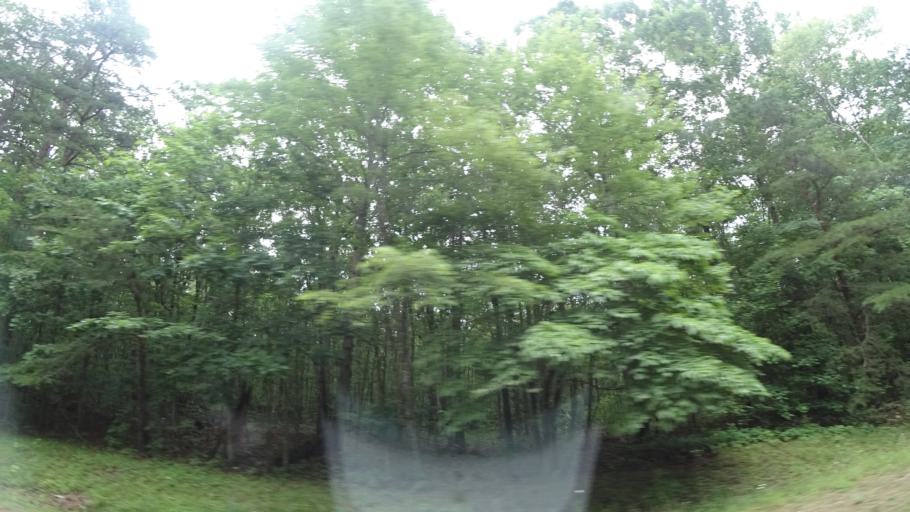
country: US
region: Virginia
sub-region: Louisa County
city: Louisa
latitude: 38.1295
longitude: -77.8195
